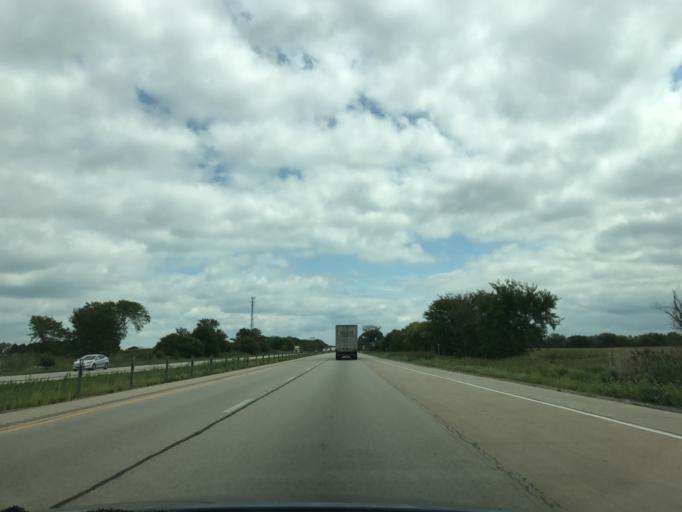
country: US
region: Illinois
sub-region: LaSalle County
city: Marseilles
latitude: 41.3753
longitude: -88.6992
